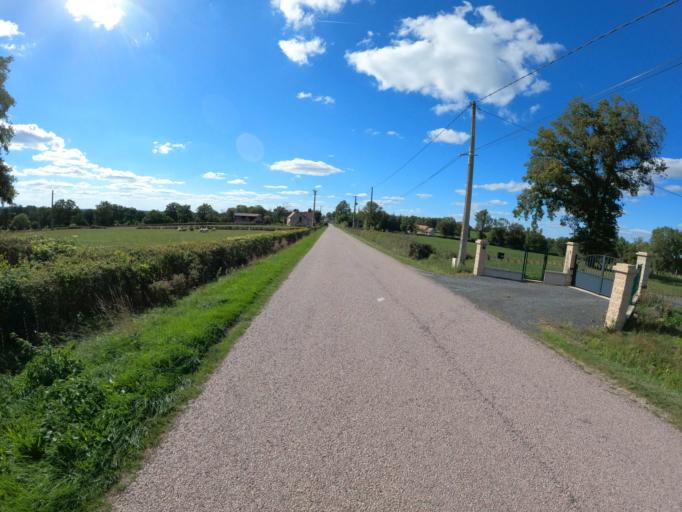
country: FR
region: Auvergne
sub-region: Departement de l'Allier
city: Buxieres-les-Mines
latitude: 46.4055
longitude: 3.0419
